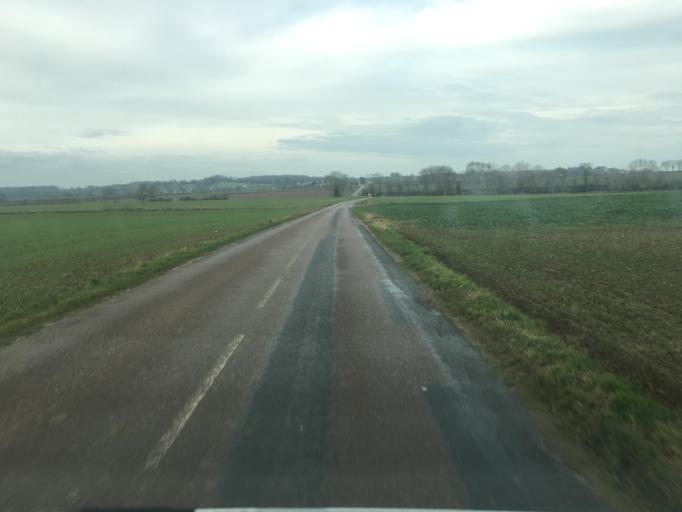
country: FR
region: Lower Normandy
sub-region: Departement du Calvados
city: Ver-sur-Mer
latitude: 49.3285
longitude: -0.5826
